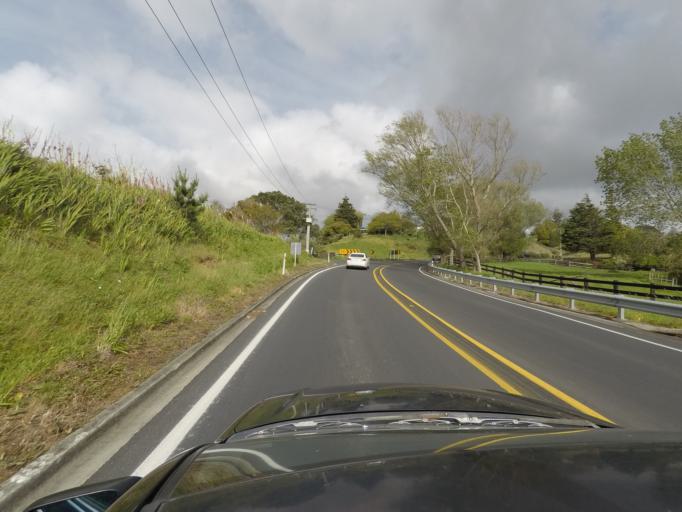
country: NZ
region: Auckland
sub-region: Auckland
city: Pakuranga
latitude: -36.9299
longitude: 174.9370
